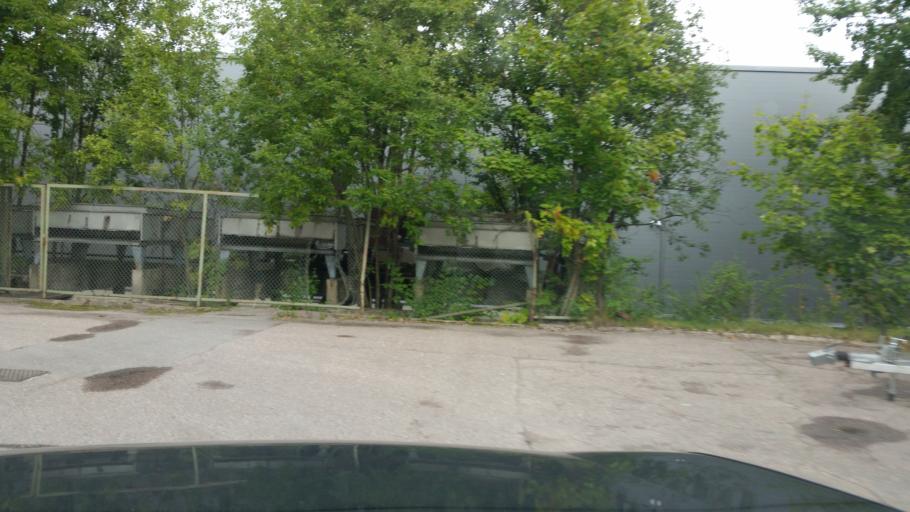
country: FI
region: Uusimaa
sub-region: Helsinki
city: Helsinki
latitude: 60.2344
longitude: 24.9766
